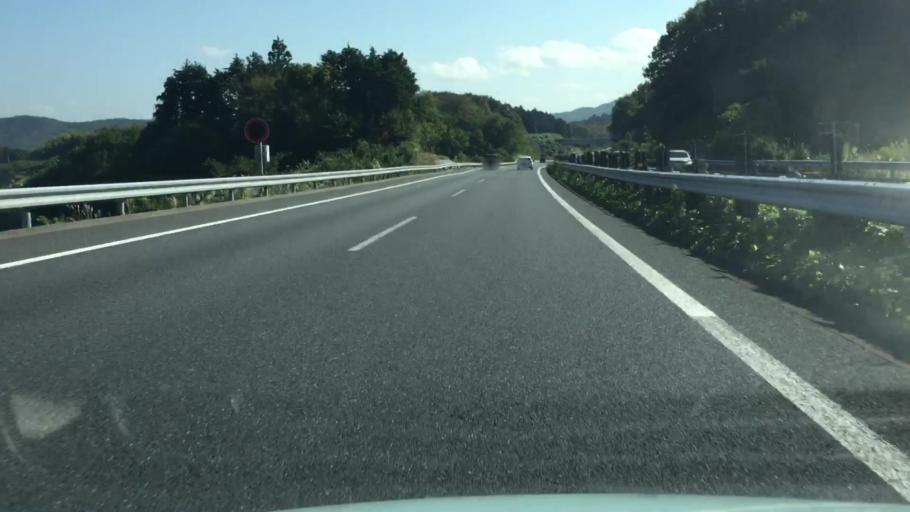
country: JP
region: Ibaraki
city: Kasama
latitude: 36.3433
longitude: 140.2033
